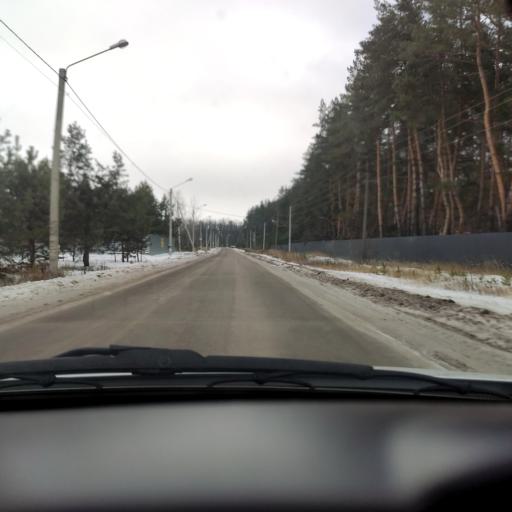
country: RU
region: Voronezj
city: Ramon'
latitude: 51.8925
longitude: 39.2741
